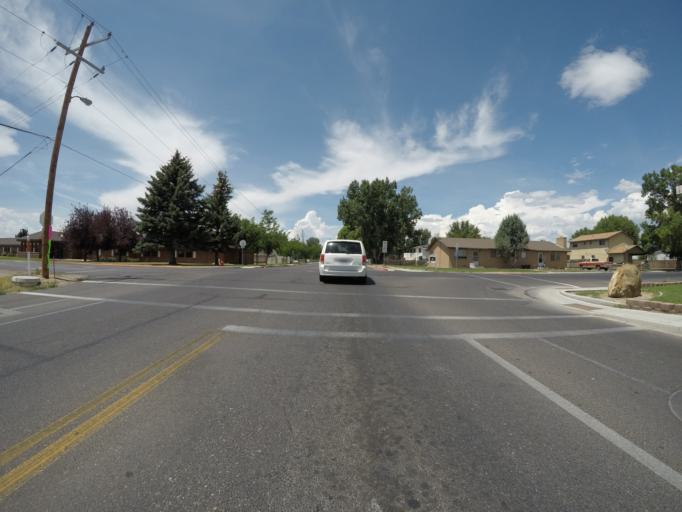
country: US
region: Utah
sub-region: Uintah County
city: Vernal
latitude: 40.4484
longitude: -109.5378
